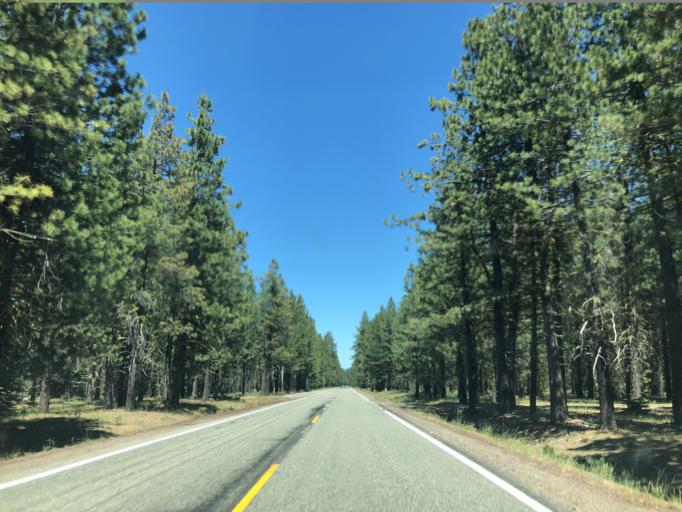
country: US
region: California
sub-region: Shasta County
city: Burney
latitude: 40.6037
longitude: -121.5280
